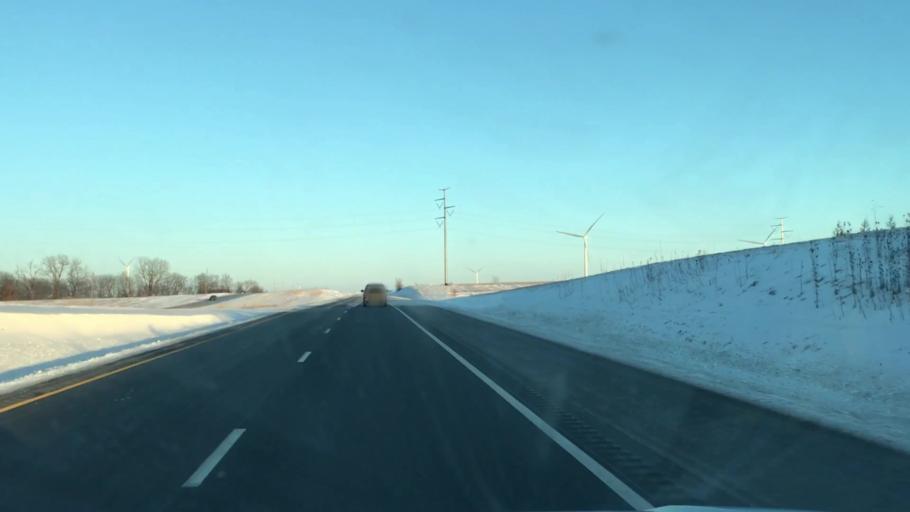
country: US
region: Missouri
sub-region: DeKalb County
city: Maysville
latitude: 39.7618
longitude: -94.4476
